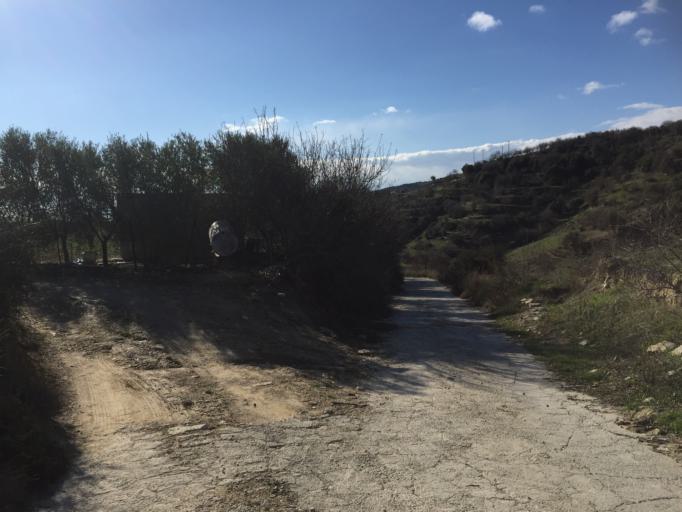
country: CY
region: Pafos
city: Mesogi
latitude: 34.8364
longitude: 32.5125
